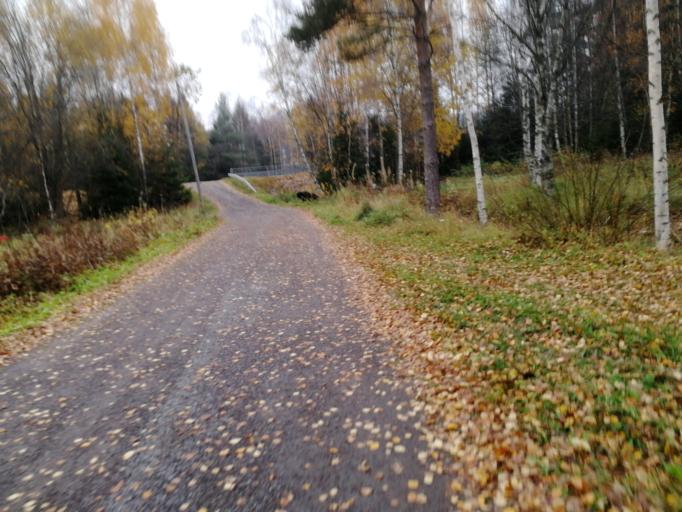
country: FI
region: Pirkanmaa
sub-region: Tampere
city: Tampere
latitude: 61.4525
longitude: 23.8889
